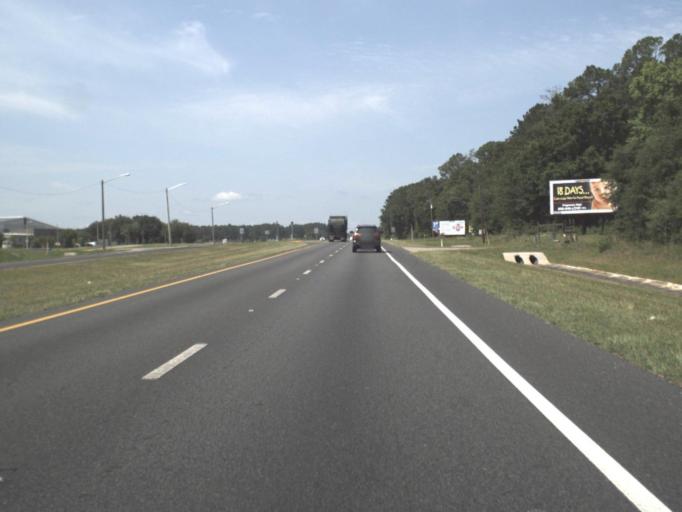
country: US
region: Florida
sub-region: Alachua County
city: Gainesville
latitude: 29.6981
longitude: -82.2805
